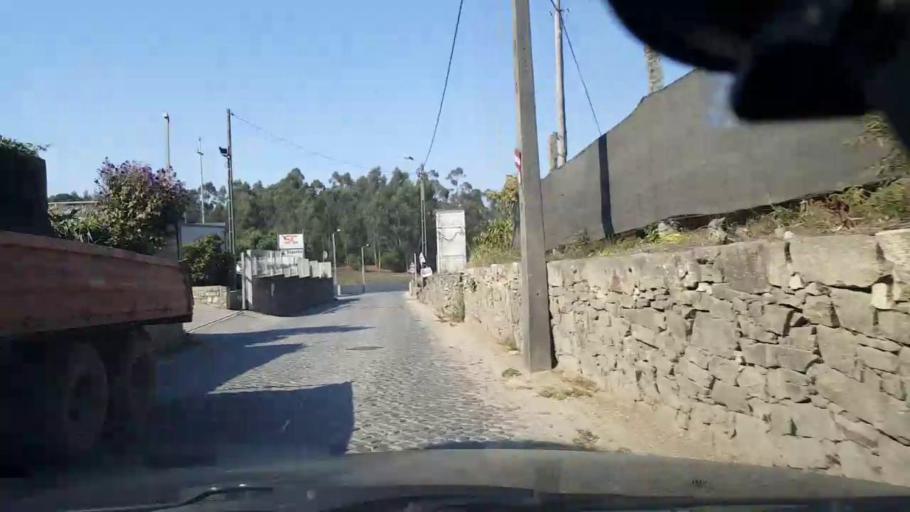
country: PT
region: Porto
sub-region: Vila do Conde
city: Arvore
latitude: 41.3859
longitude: -8.6861
